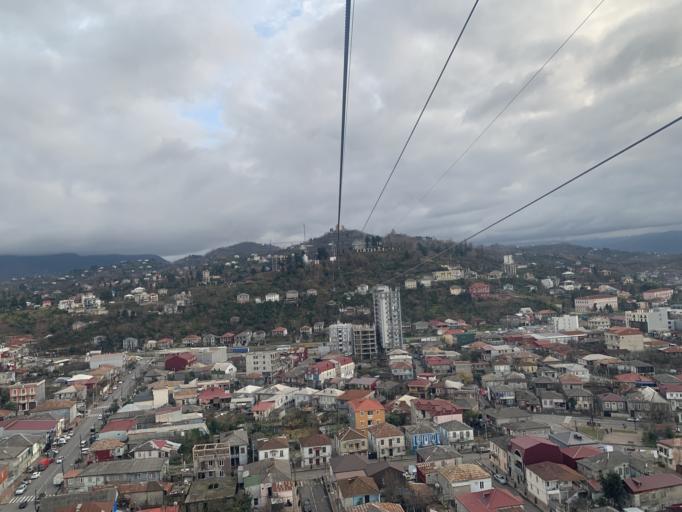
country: GE
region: Ajaria
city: Batumi
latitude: 41.6428
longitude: 41.6480
